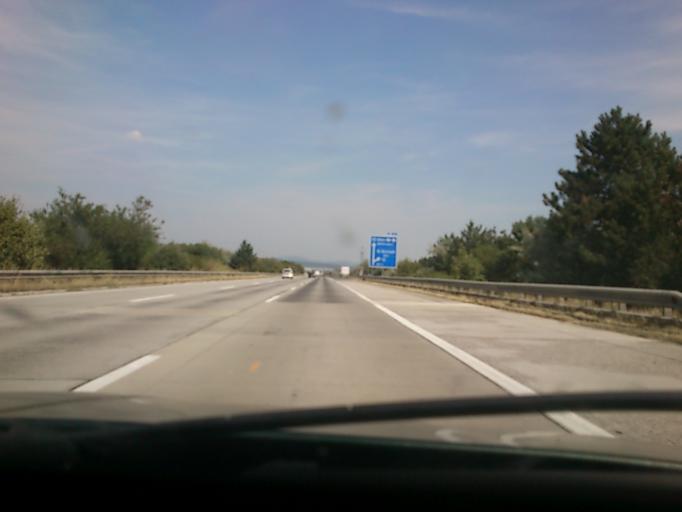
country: AT
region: Lower Austria
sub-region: Wiener Neustadt Stadt
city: Wiener Neustadt
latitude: 47.7902
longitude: 16.2045
